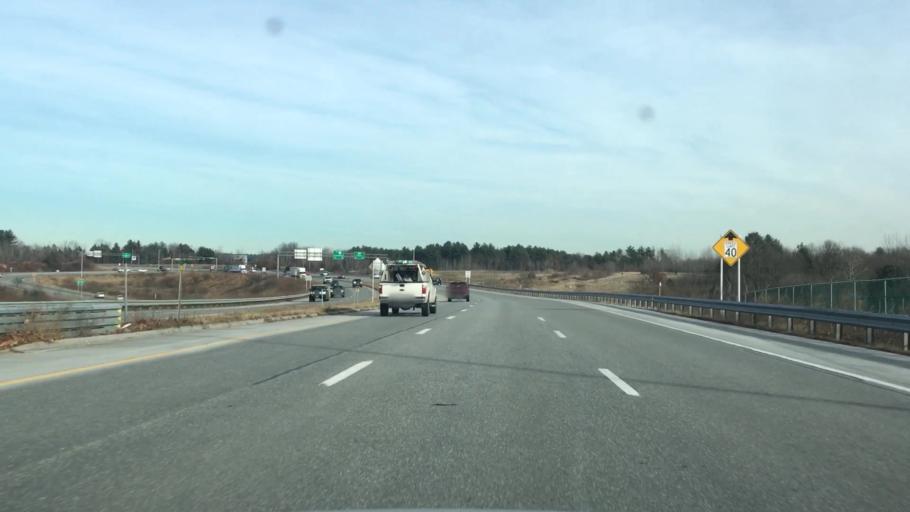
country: US
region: New Hampshire
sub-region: Hillsborough County
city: East Merrimack
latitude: 42.9140
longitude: -71.4501
